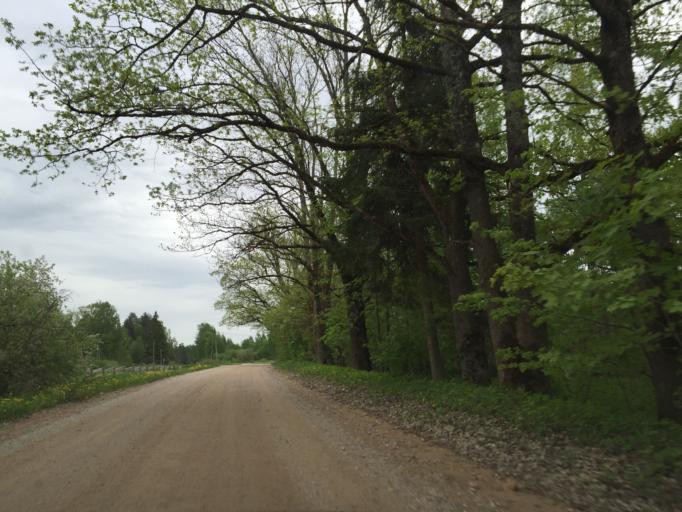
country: LV
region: Lielvarde
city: Lielvarde
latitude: 56.8055
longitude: 24.8414
